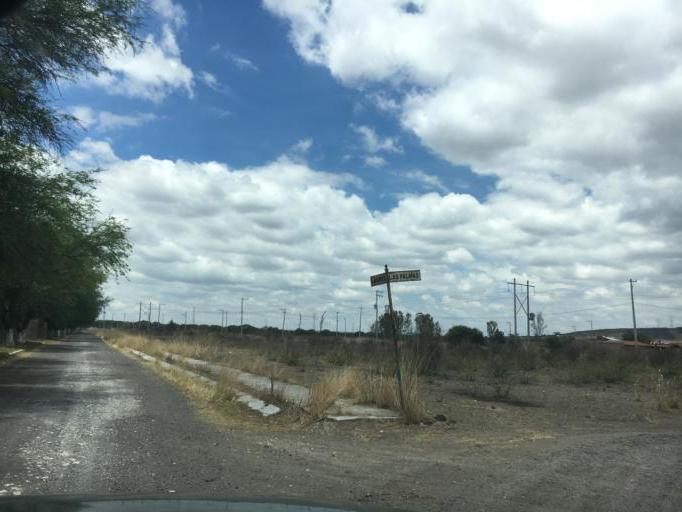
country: MX
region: Guanajuato
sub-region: Leon
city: Plan Guanajuato (La Sandia)
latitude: 20.9227
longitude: -101.7499
